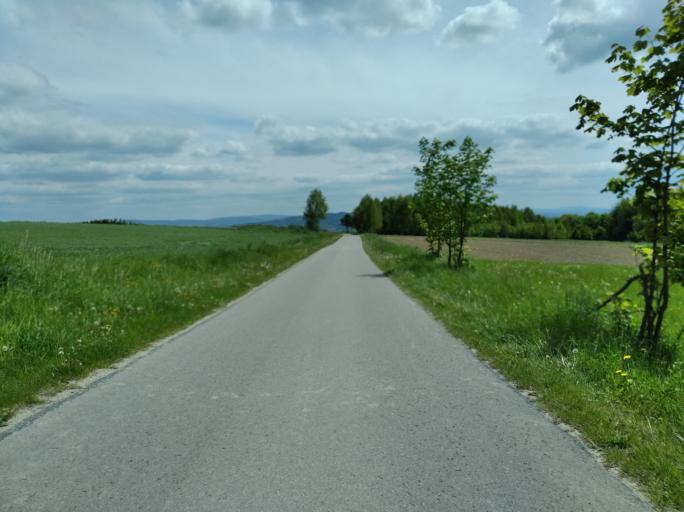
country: PL
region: Subcarpathian Voivodeship
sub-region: Powiat ropczycko-sedziszowski
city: Wielopole Skrzynskie
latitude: 49.8998
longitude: 21.6093
